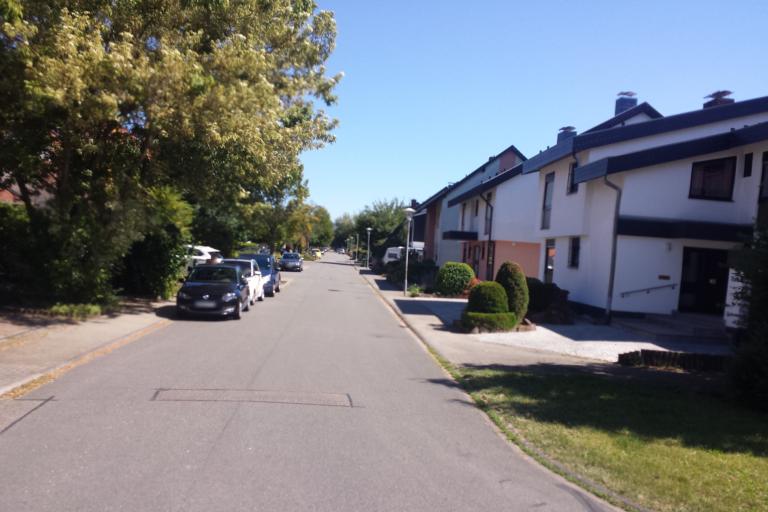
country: DE
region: Baden-Wuerttemberg
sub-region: Karlsruhe Region
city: Plankstadt
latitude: 49.4012
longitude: 8.5840
